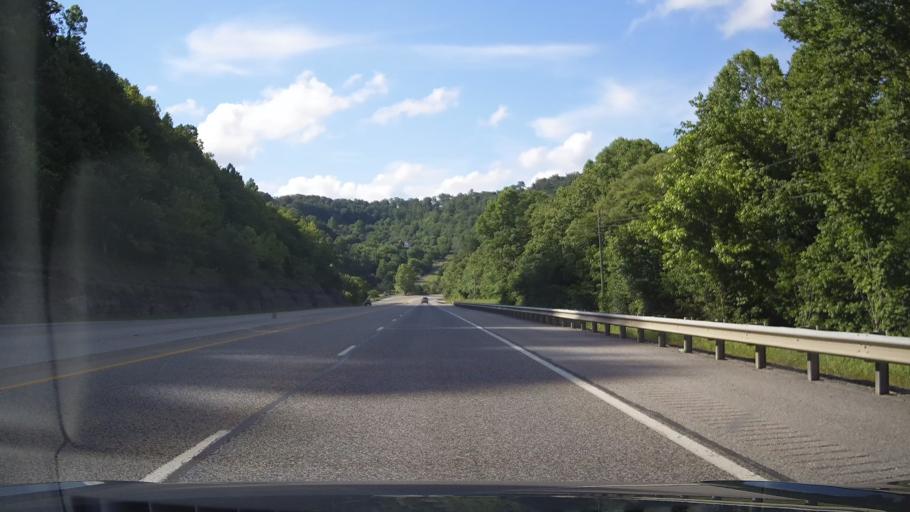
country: US
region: Kentucky
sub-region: Lawrence County
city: Louisa
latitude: 38.0043
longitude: -82.6641
